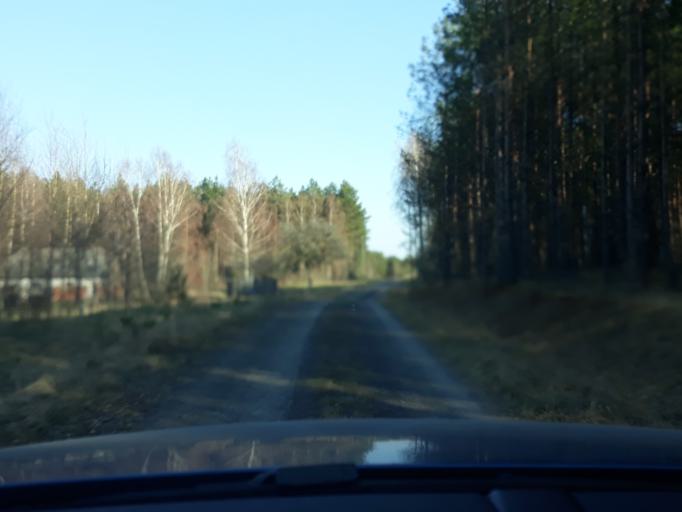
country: PL
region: Pomeranian Voivodeship
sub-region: Powiat bytowski
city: Lipnica
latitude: 53.9125
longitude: 17.4959
